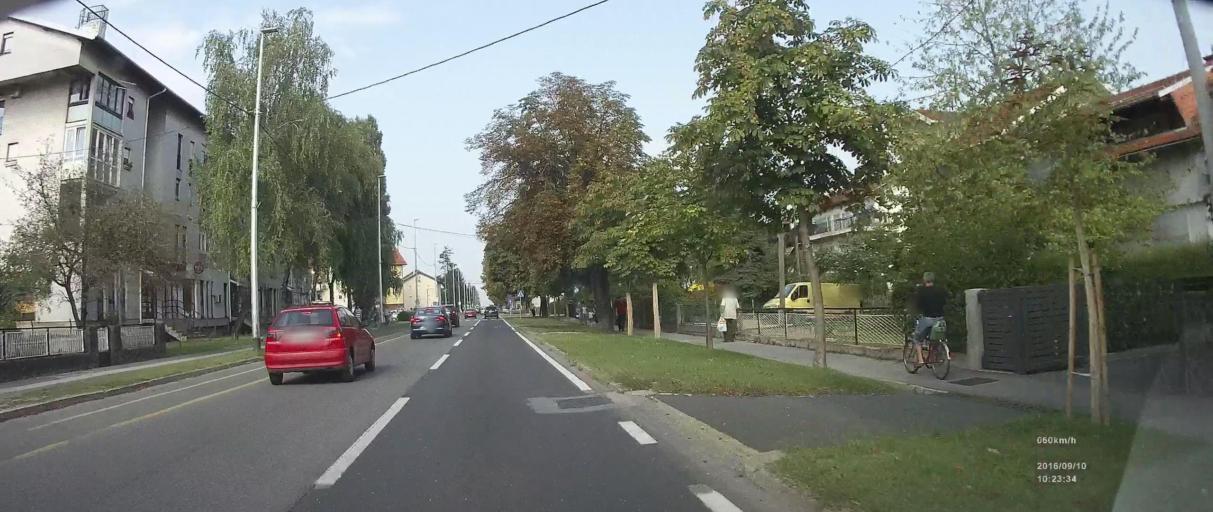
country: HR
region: Zagrebacka
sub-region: Grad Velika Gorica
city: Velika Gorica
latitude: 45.7181
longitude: 16.0637
